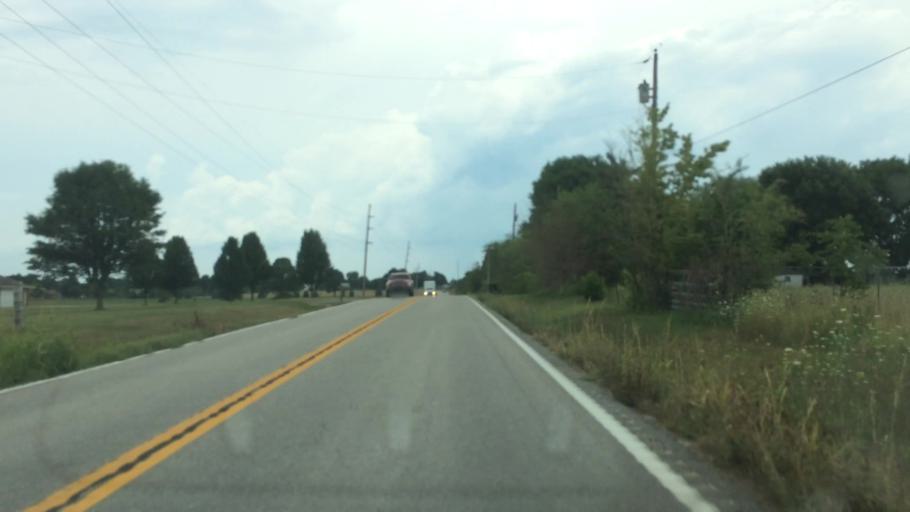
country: US
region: Missouri
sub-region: Greene County
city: Strafford
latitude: 37.2464
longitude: -93.1354
